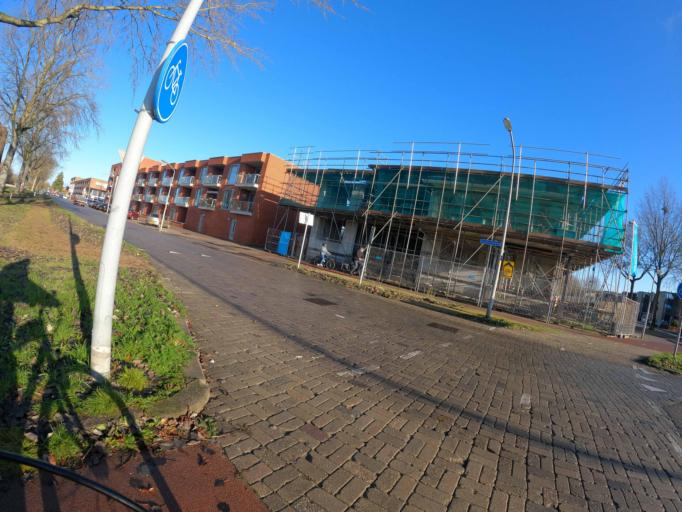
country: NL
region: Flevoland
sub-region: Gemeente Zeewolde
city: Zeewolde
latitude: 52.3295
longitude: 5.5388
